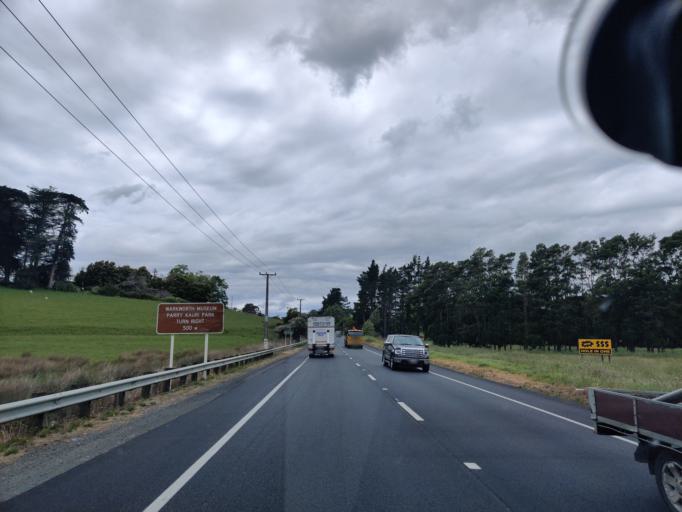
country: NZ
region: Auckland
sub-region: Auckland
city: Warkworth
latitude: -36.4168
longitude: 174.6539
